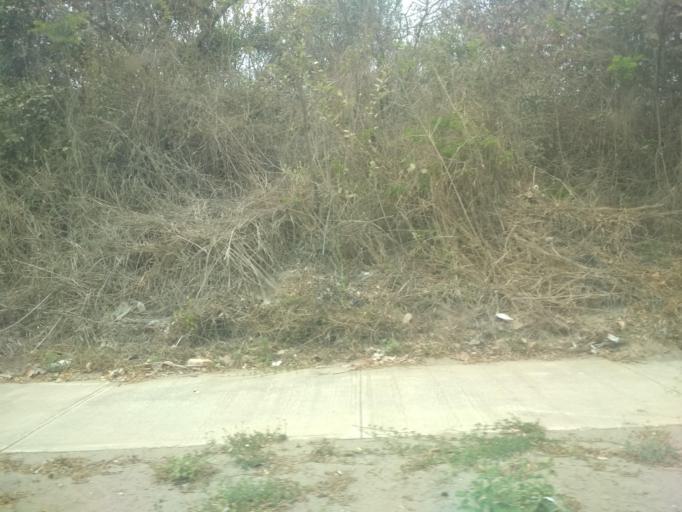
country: MX
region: Veracruz
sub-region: Alvarado
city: Playa de la Libertad
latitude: 19.0570
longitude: -96.0636
